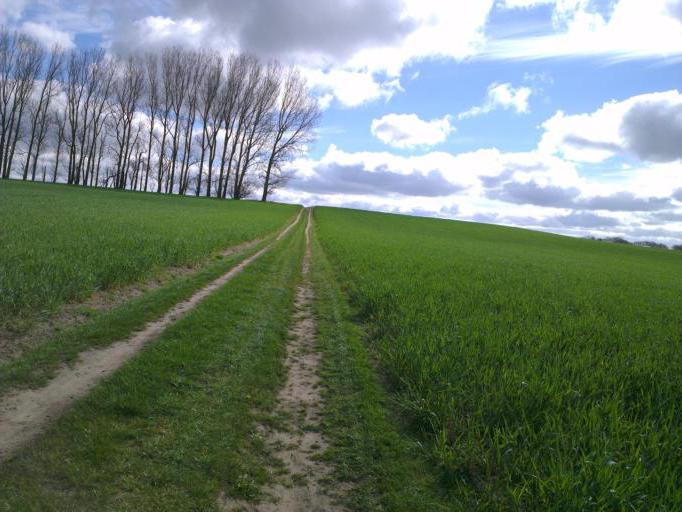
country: DK
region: Capital Region
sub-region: Frederikssund Kommune
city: Jaegerspris
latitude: 55.8109
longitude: 12.0033
